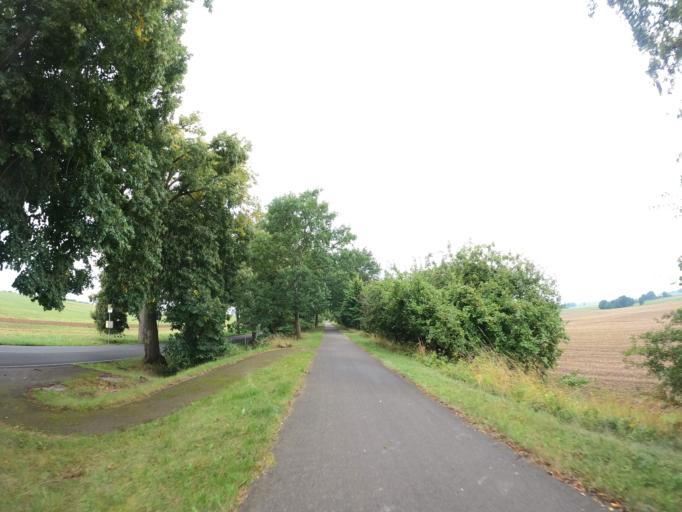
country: DE
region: Mecklenburg-Vorpommern
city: Poseritz
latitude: 54.2951
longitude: 13.2976
